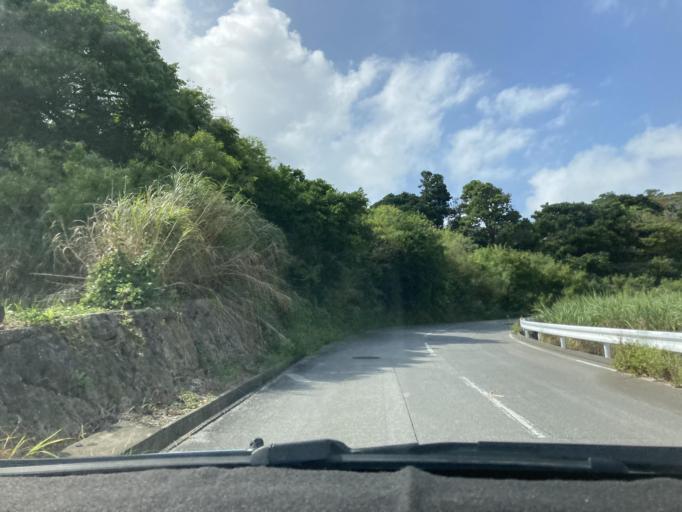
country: JP
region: Okinawa
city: Ginowan
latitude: 26.1528
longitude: 127.8040
